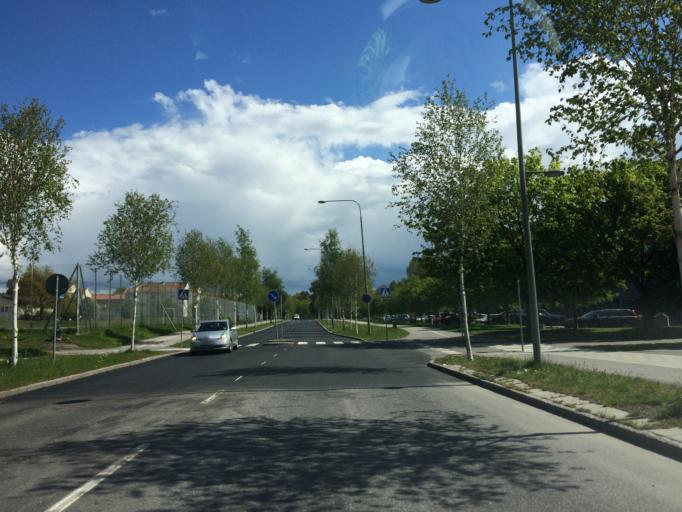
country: SE
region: Stockholm
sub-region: Huddinge Kommun
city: Segeltorp
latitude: 59.2831
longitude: 17.9596
